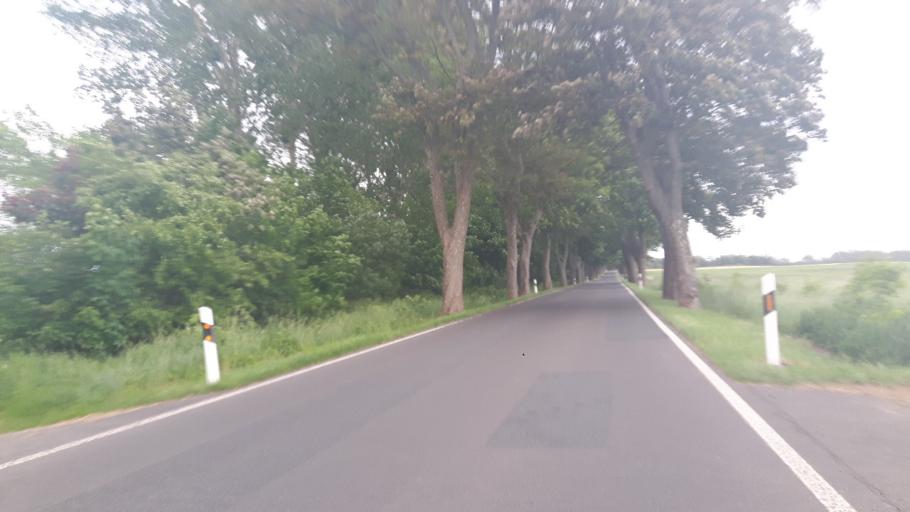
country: DE
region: Brandenburg
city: Eberswalde
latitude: 52.7729
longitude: 13.8469
